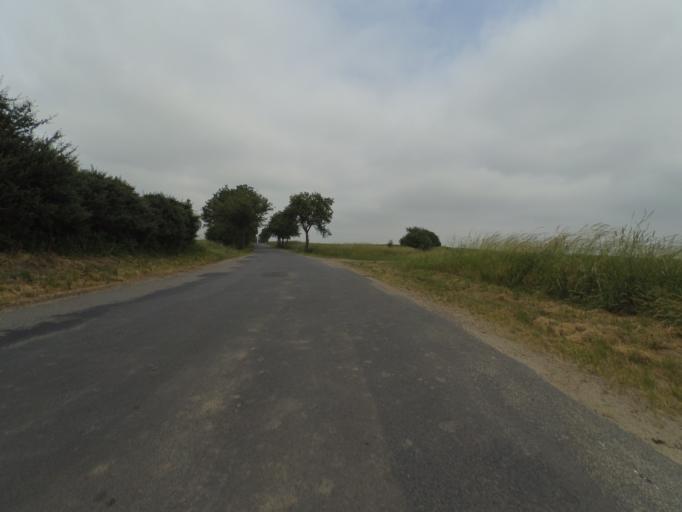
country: DE
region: Mecklenburg-Vorpommern
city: Goldberg
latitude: 53.5156
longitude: 12.1117
